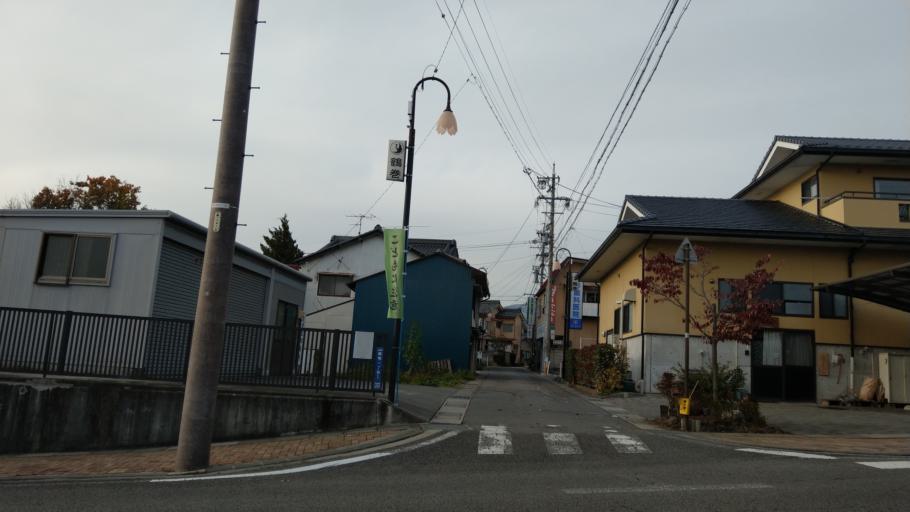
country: JP
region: Nagano
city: Komoro
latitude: 36.3243
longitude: 138.4286
